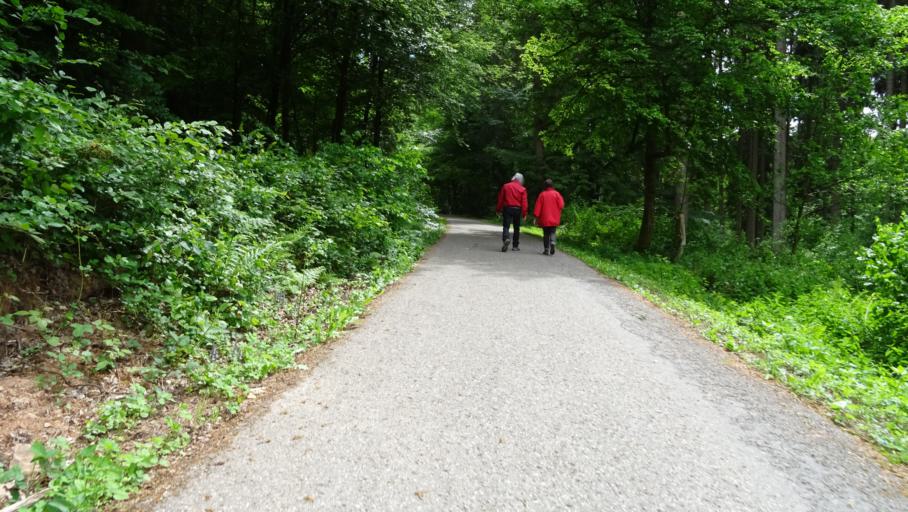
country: DE
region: Baden-Wuerttemberg
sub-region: Karlsruhe Region
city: Fahrenbach
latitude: 49.3931
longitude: 9.1752
